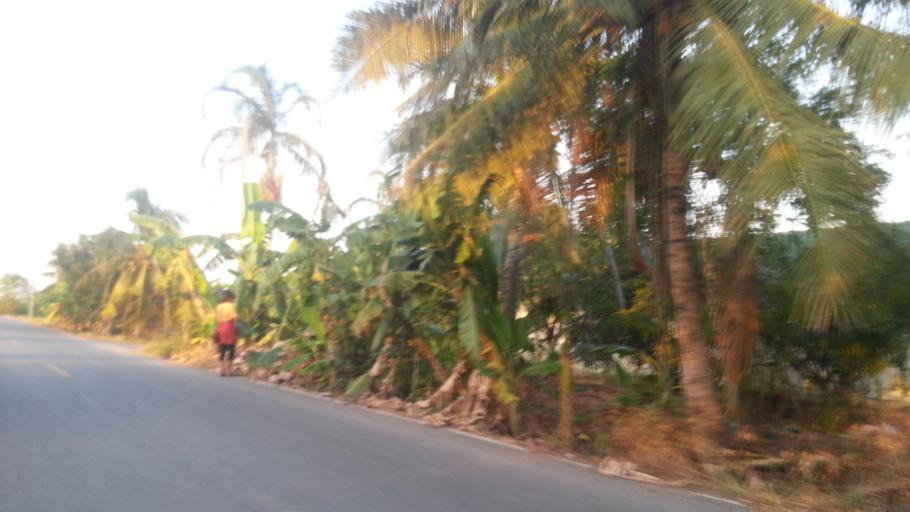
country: TH
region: Pathum Thani
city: Nong Suea
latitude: 14.0499
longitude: 100.8672
